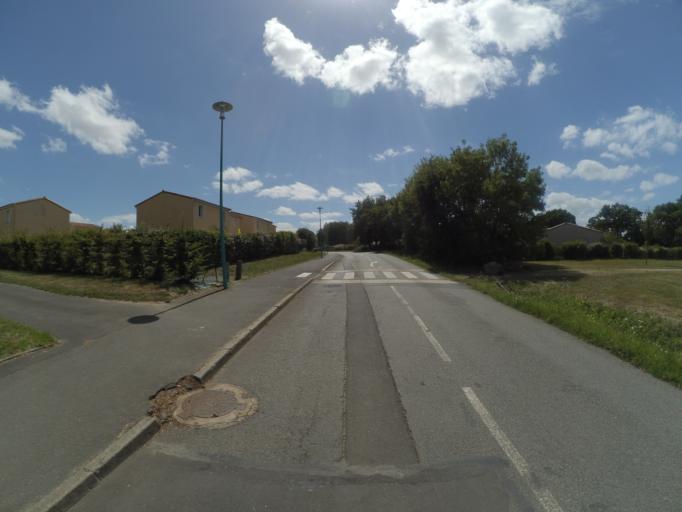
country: FR
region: Pays de la Loire
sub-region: Departement de la Loire-Atlantique
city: Aigrefeuille-sur-Maine
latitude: 47.0716
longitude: -1.4007
